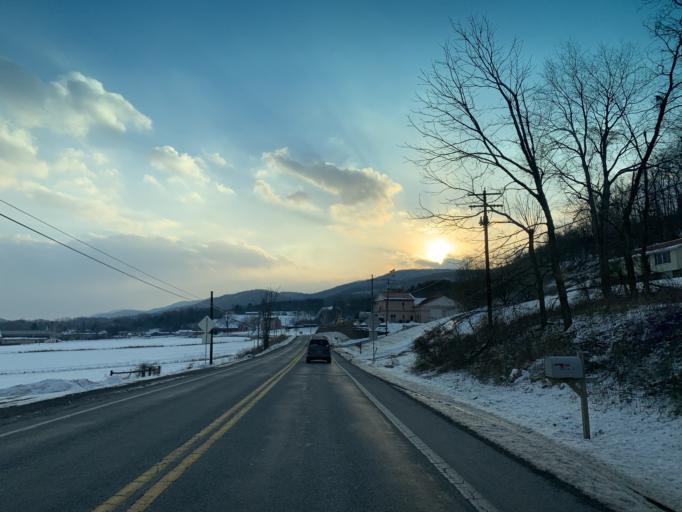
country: US
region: Maryland
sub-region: Allegany County
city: Cumberland
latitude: 39.7300
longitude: -78.7695
